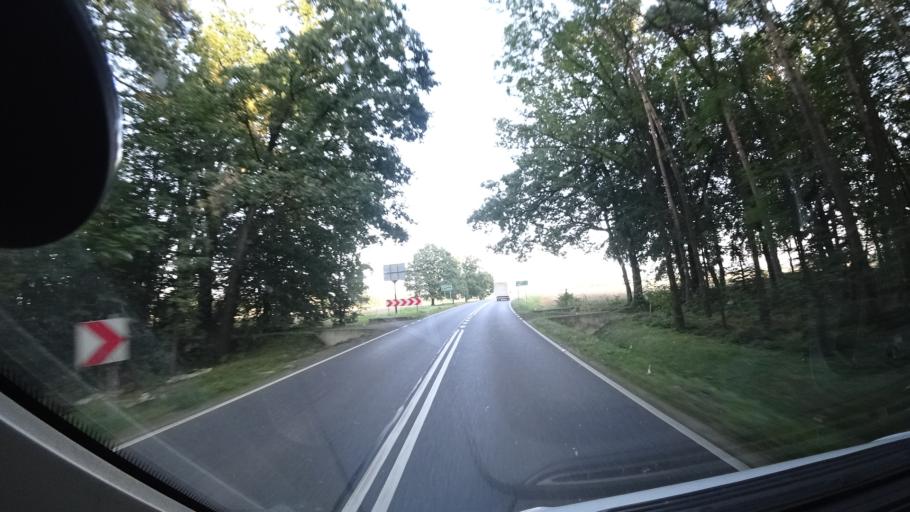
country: PL
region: Silesian Voivodeship
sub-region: Powiat gliwicki
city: Sosnicowice
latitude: 50.2793
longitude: 18.5095
